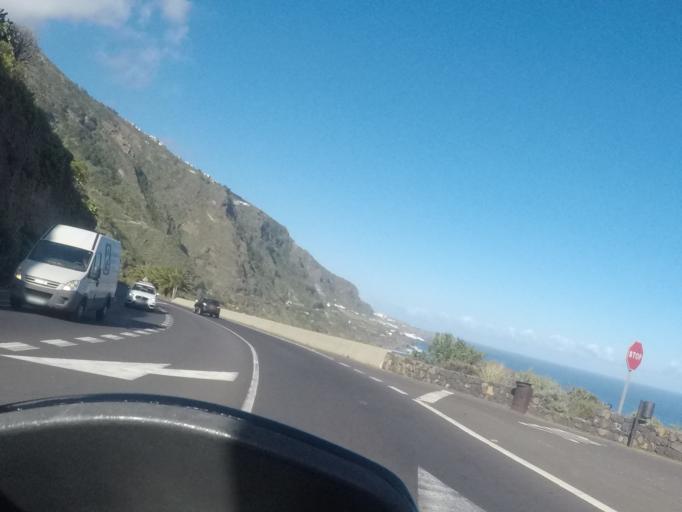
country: ES
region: Canary Islands
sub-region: Provincia de Santa Cruz de Tenerife
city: Realejo Alto
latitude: 28.3952
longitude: -16.5946
